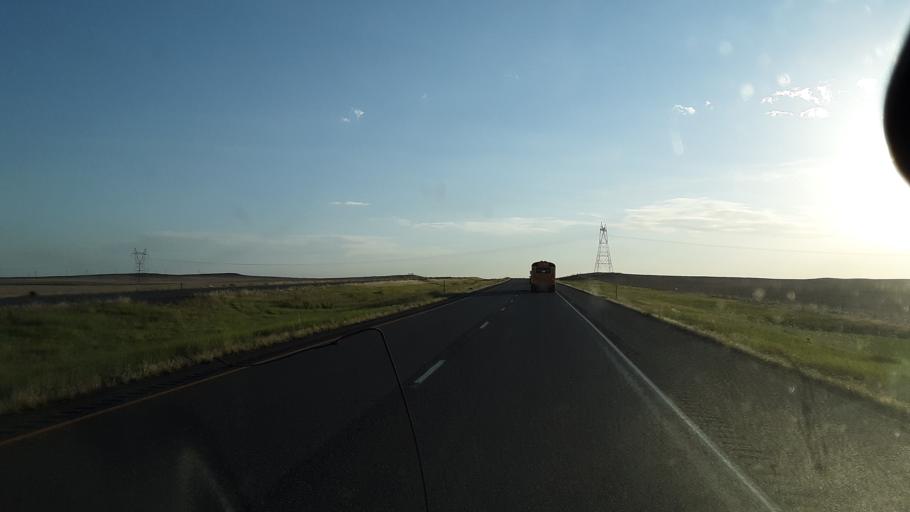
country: US
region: Montana
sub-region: Big Horn County
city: Hardin
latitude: 45.7463
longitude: -107.6875
